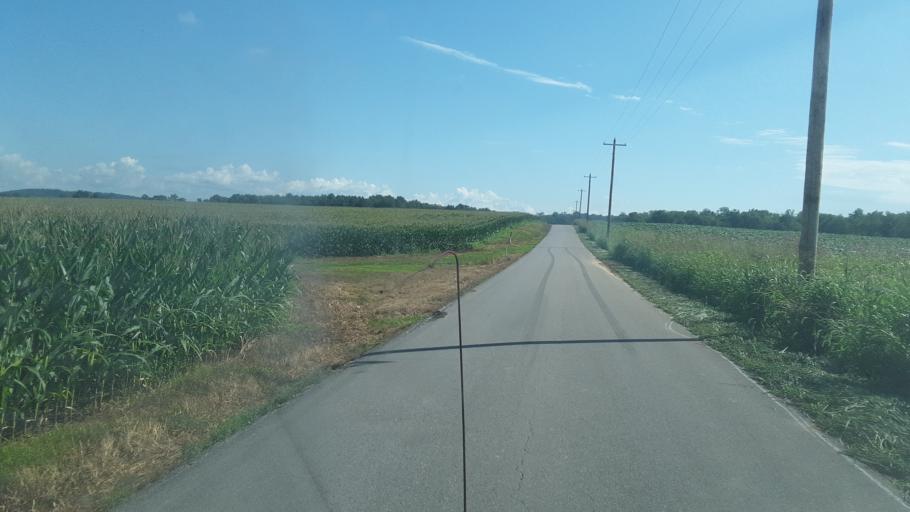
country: US
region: Kentucky
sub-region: Todd County
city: Elkton
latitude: 36.7896
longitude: -87.2093
